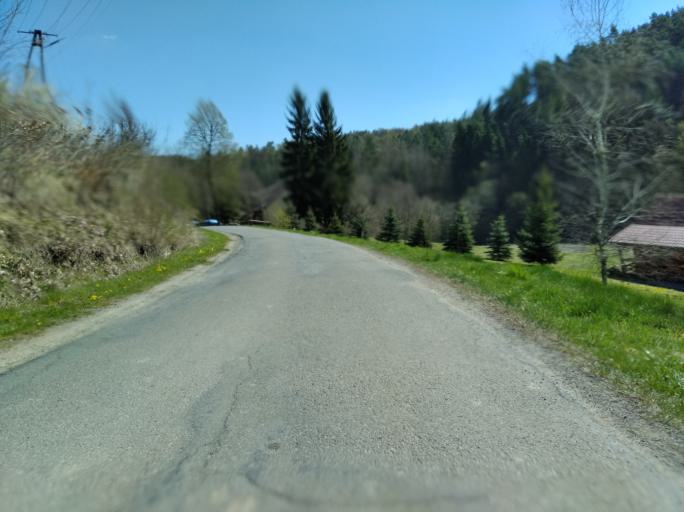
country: PL
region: Subcarpathian Voivodeship
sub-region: Powiat brzozowski
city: Dydnia
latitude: 49.7135
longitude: 22.1765
